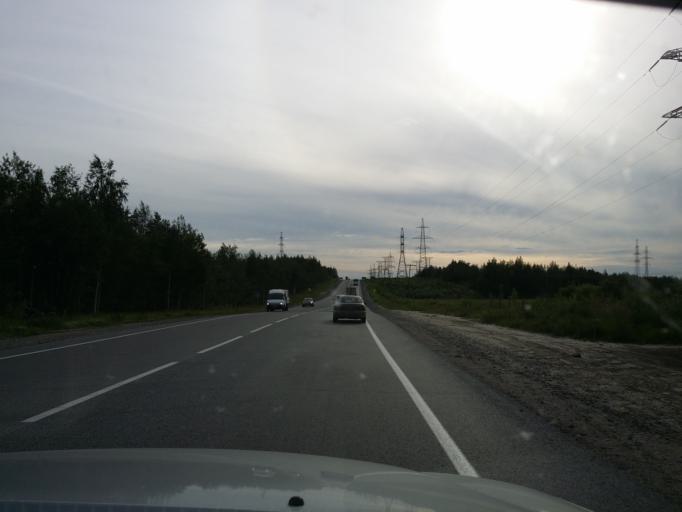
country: RU
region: Khanty-Mansiyskiy Avtonomnyy Okrug
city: Nizhnevartovsk
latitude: 60.9675
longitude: 76.6765
